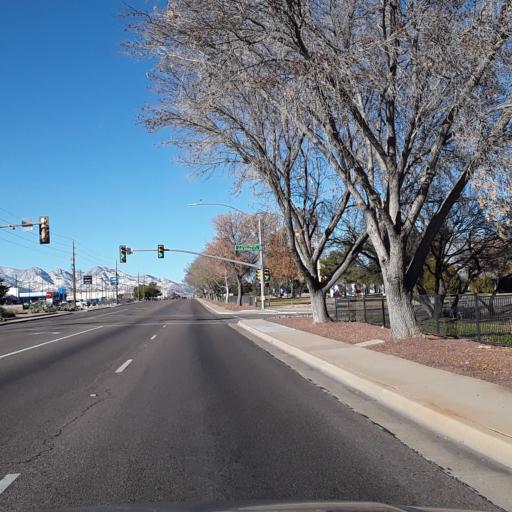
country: US
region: Arizona
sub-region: Cochise County
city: Sierra Vista
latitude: 31.5547
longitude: -110.2663
